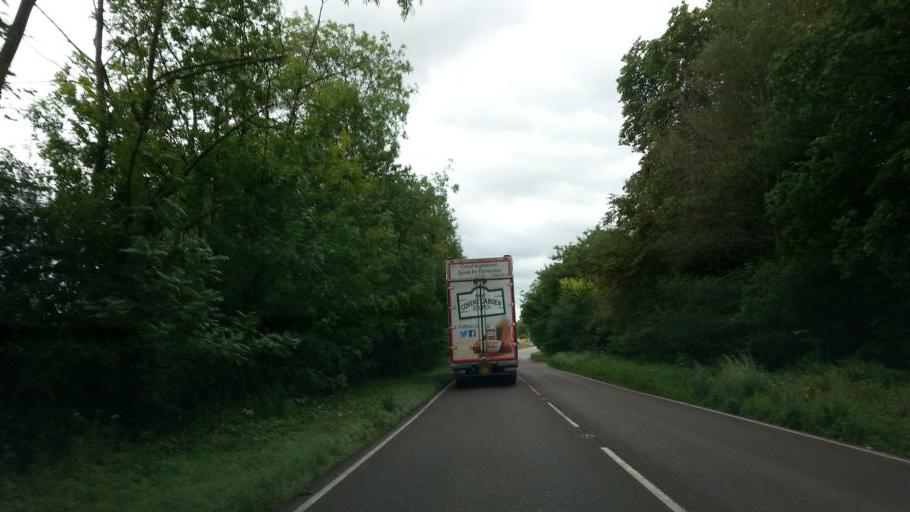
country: GB
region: England
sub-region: Cambridgeshire
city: Papworth Everard
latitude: 52.2595
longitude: -0.1254
